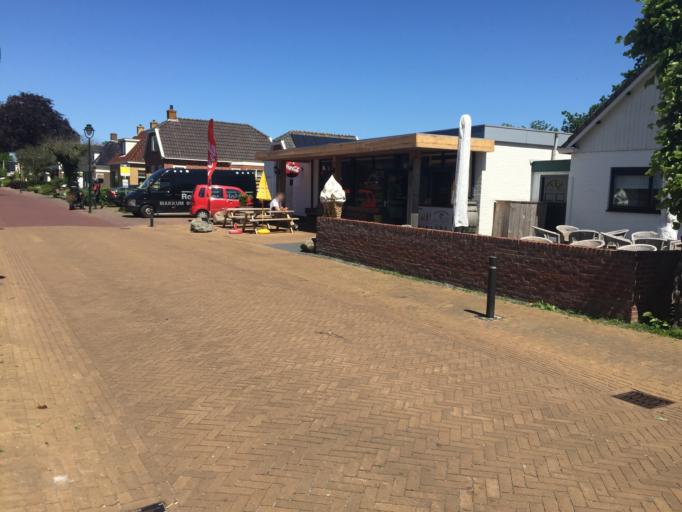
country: NL
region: Friesland
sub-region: Gemeente Smallingerland
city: Boornbergum
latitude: 53.0829
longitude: 6.0458
